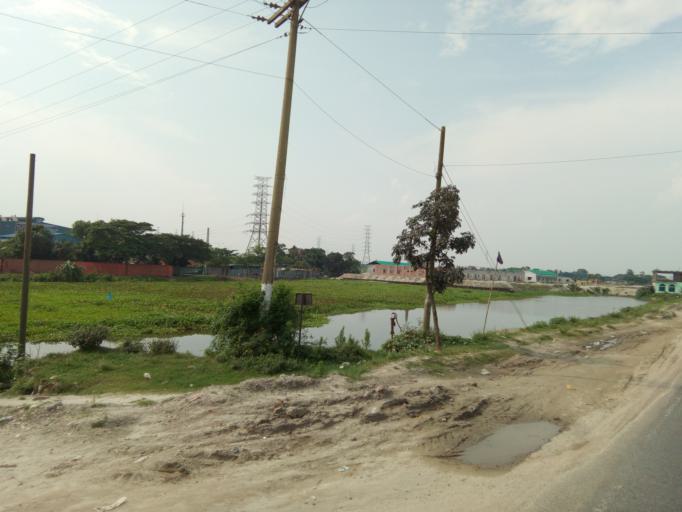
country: BD
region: Dhaka
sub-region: Dhaka
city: Dhaka
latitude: 23.6463
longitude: 90.3493
